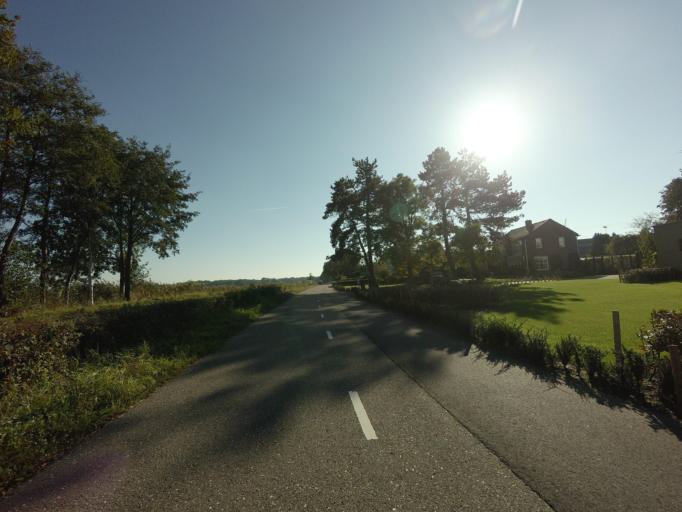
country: NL
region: North Holland
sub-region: Gemeente Wijdemeren
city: Kortenhoef
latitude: 52.2684
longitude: 5.1218
